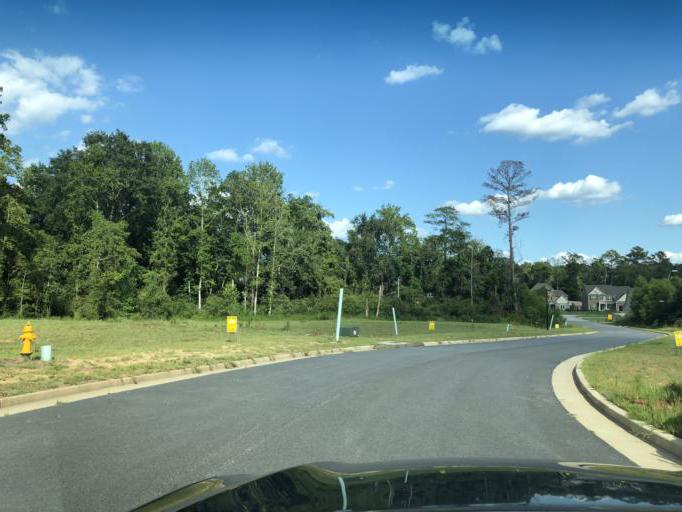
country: US
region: Georgia
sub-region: Muscogee County
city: Columbus
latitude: 32.5000
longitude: -84.9080
